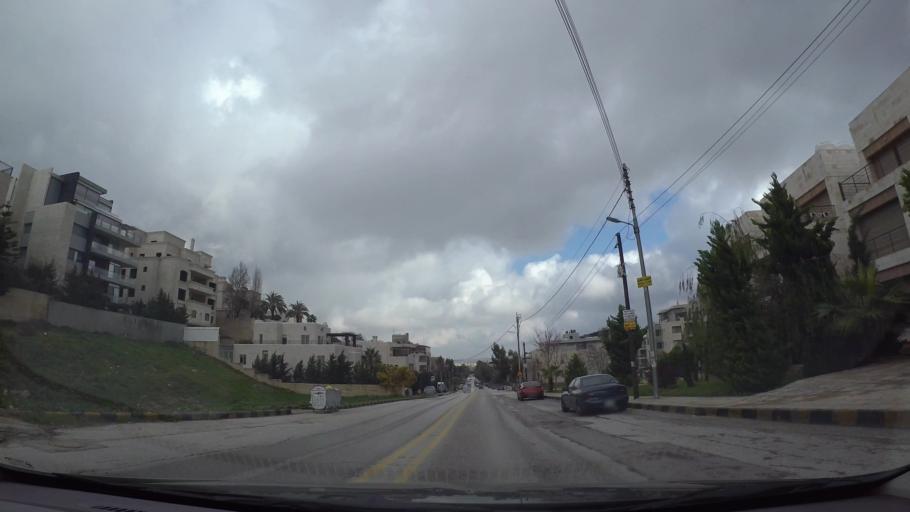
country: JO
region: Amman
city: Al Bunayyat ash Shamaliyah
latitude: 31.9482
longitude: 35.8836
